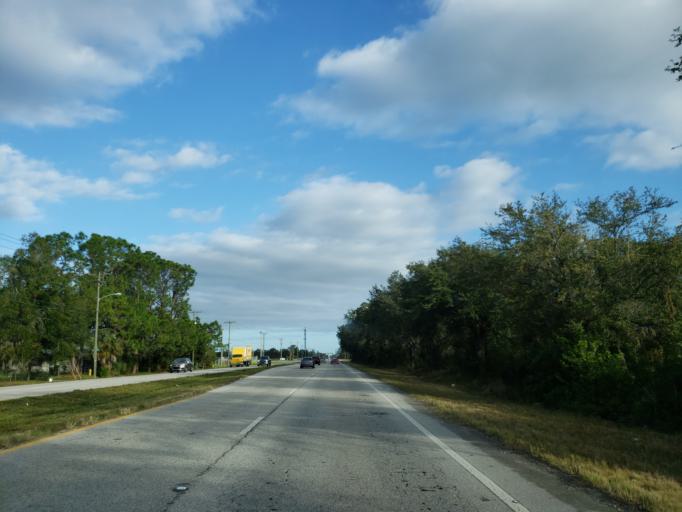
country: US
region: Florida
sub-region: Hillsborough County
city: Plant City
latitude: 28.0114
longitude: -82.1048
